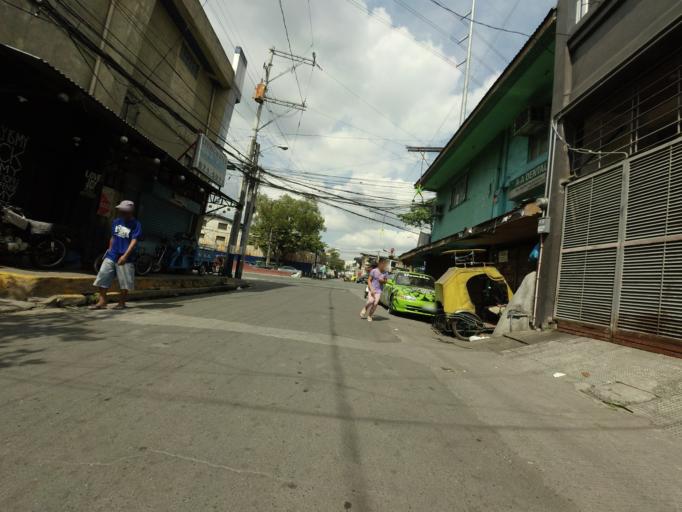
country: PH
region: Metro Manila
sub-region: City of Manila
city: Quiapo
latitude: 14.5747
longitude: 120.9954
